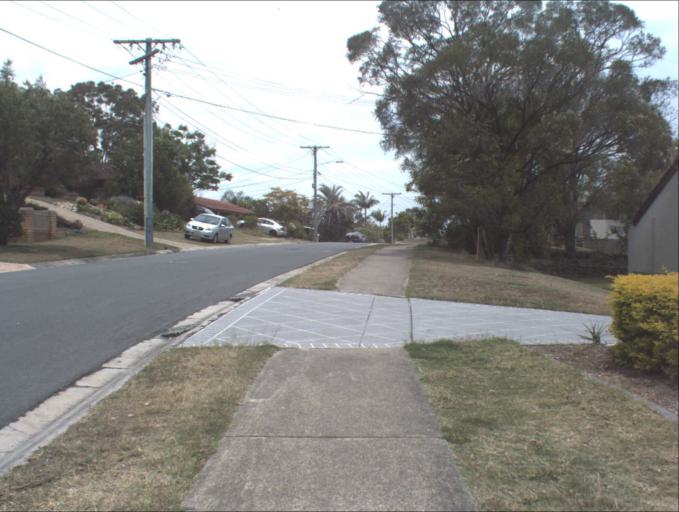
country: AU
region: Queensland
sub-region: Logan
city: Springwood
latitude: -27.6236
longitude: 153.1389
